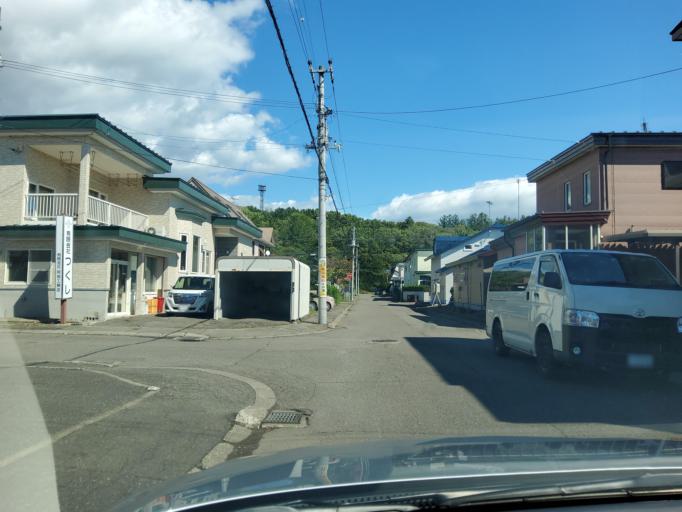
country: JP
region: Hokkaido
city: Obihiro
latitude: 42.9461
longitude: 143.2203
